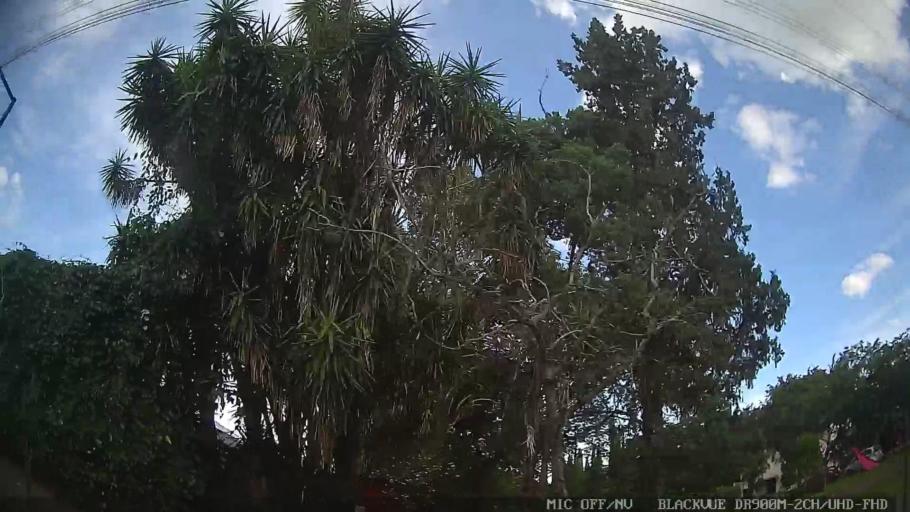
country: BR
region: Sao Paulo
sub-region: Jaguariuna
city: Jaguariuna
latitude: -22.6269
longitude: -47.0589
